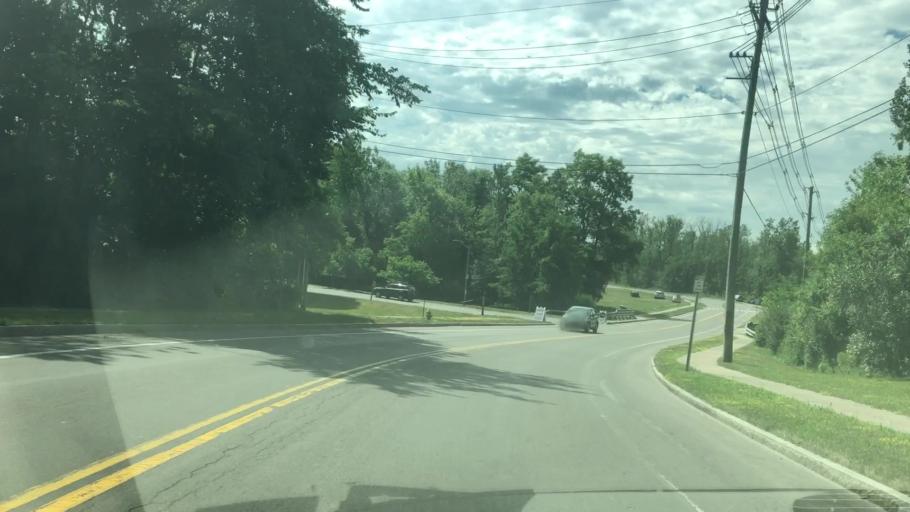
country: US
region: New York
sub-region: Monroe County
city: Fairport
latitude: 43.0924
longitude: -77.4025
